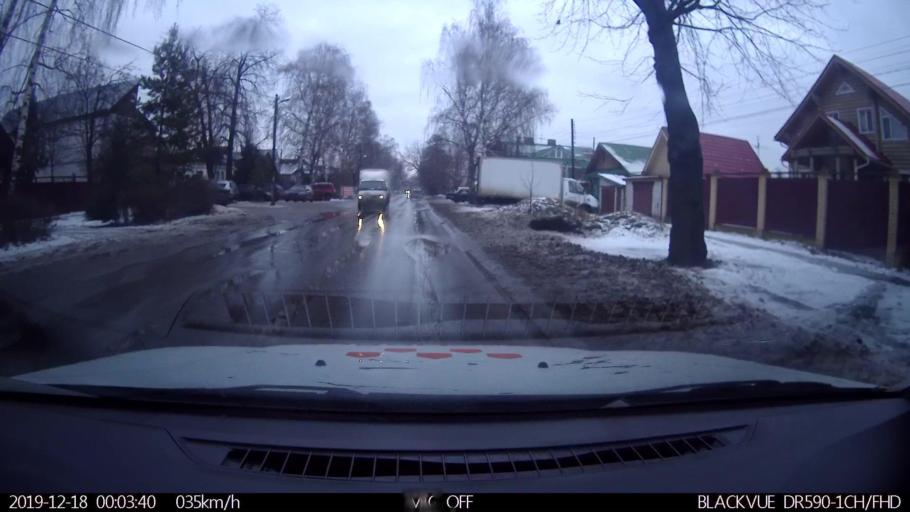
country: RU
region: Nizjnij Novgorod
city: Gorbatovka
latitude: 56.3686
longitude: 43.8378
